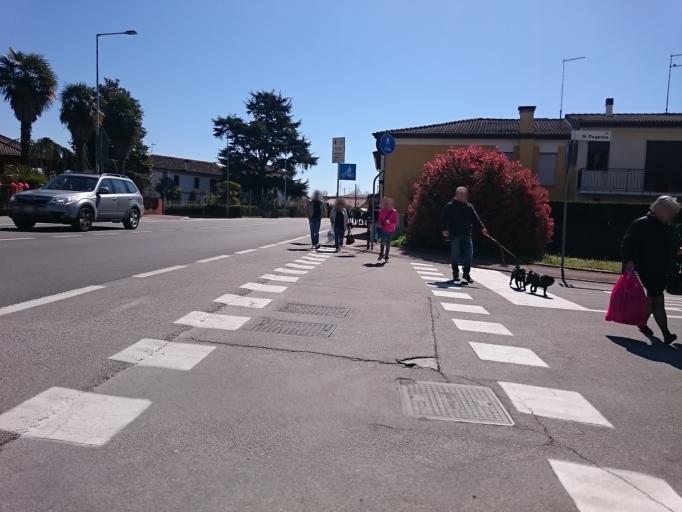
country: IT
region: Veneto
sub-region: Provincia di Padova
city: Brugine
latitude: 45.2961
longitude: 11.9952
